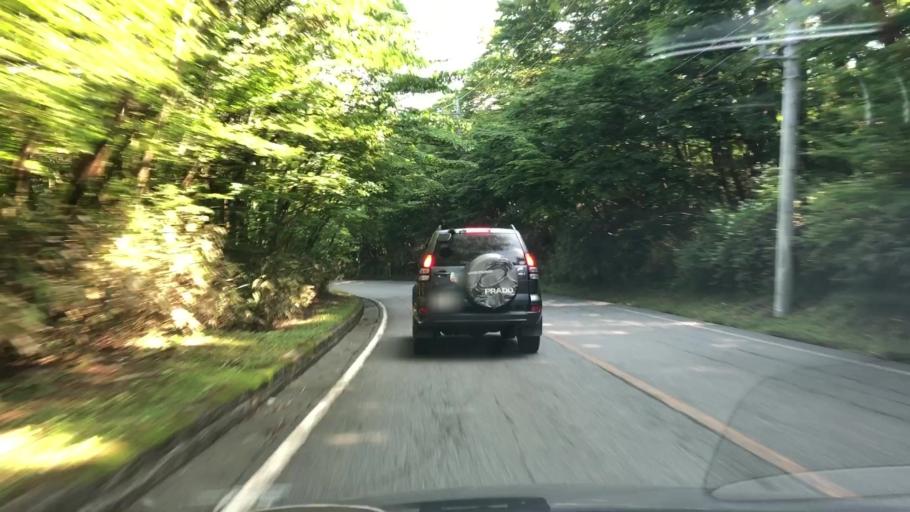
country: JP
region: Shizuoka
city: Gotemba
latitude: 35.3302
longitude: 138.8101
